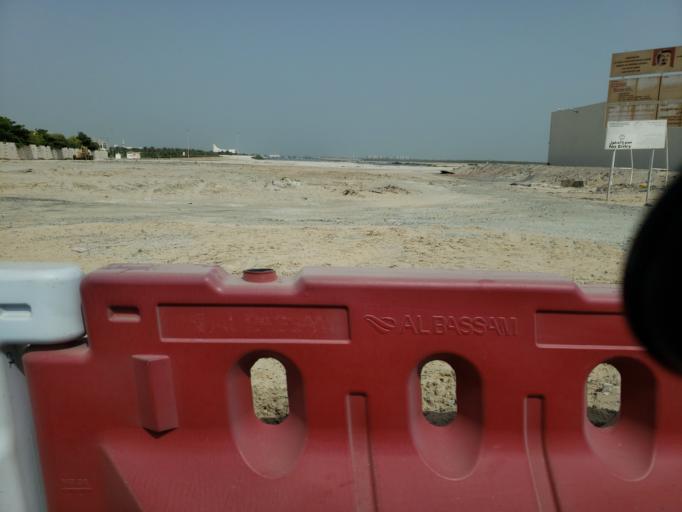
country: AE
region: Ajman
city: Ajman
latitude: 25.4168
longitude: 55.4873
